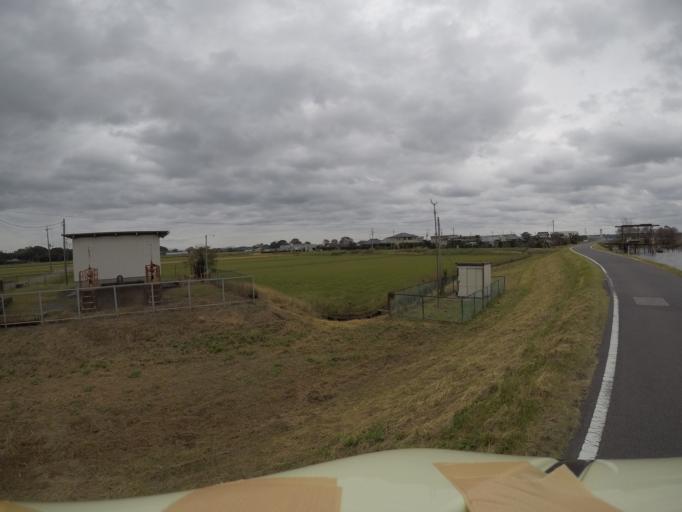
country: JP
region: Ibaraki
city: Inashiki
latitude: 36.0814
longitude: 140.3896
